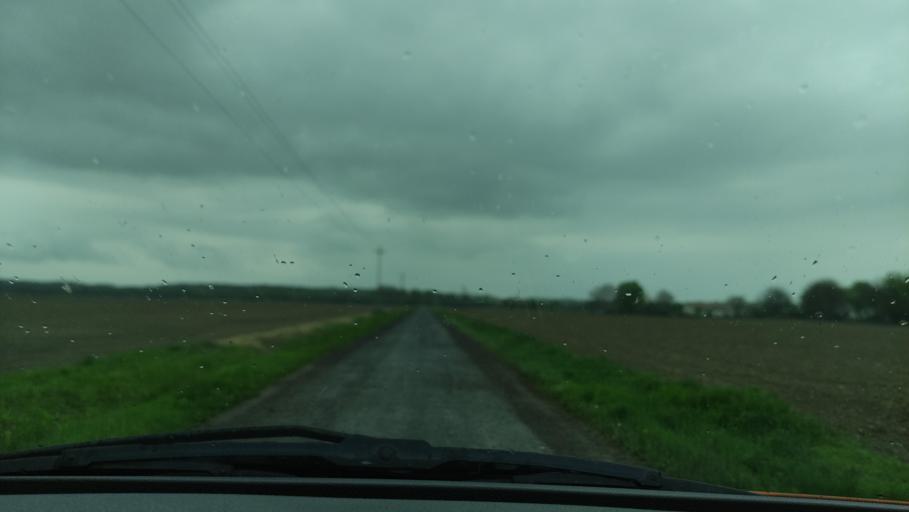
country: HR
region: Osjecko-Baranjska
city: Batina
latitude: 45.9020
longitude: 18.7738
